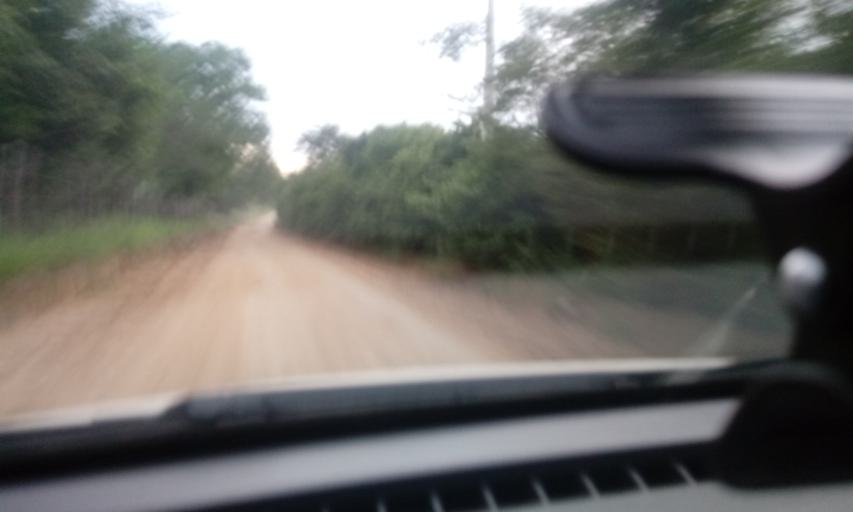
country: BR
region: Bahia
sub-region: Riacho De Santana
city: Riacho de Santana
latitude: -13.8052
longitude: -42.7552
